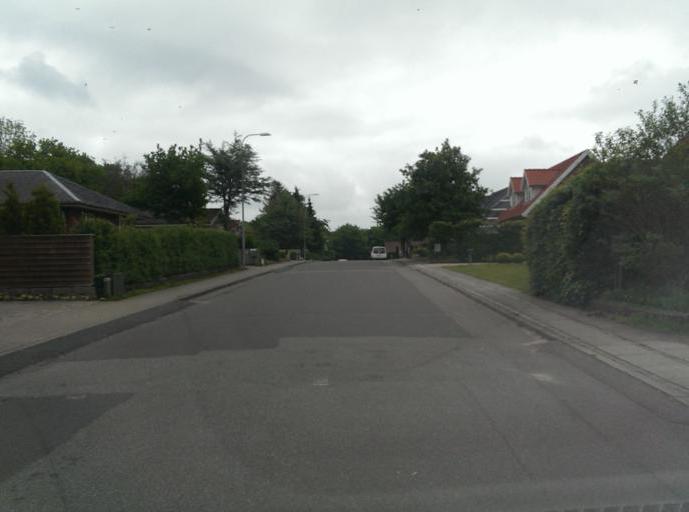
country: DK
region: South Denmark
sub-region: Fano Kommune
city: Nordby
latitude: 55.5215
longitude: 8.3643
